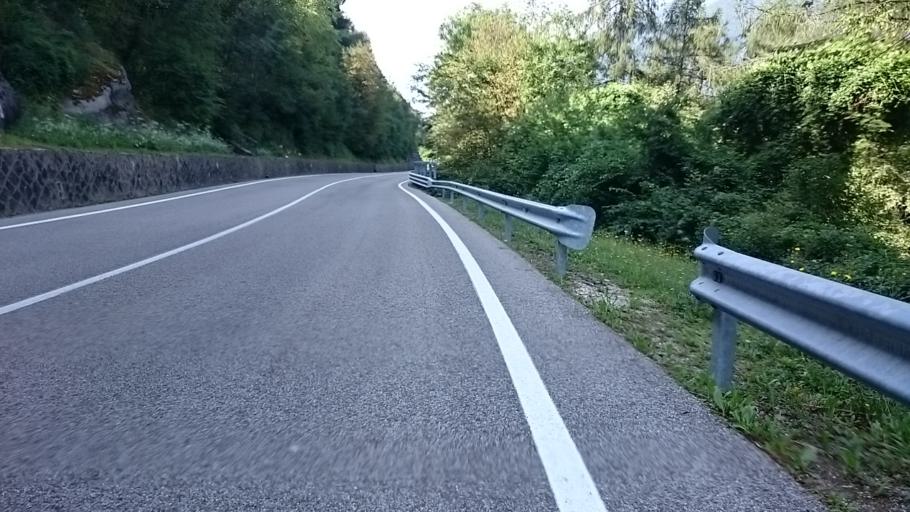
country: IT
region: Veneto
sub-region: Provincia di Belluno
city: Farra d'Alpago
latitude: 46.1011
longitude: 12.3483
